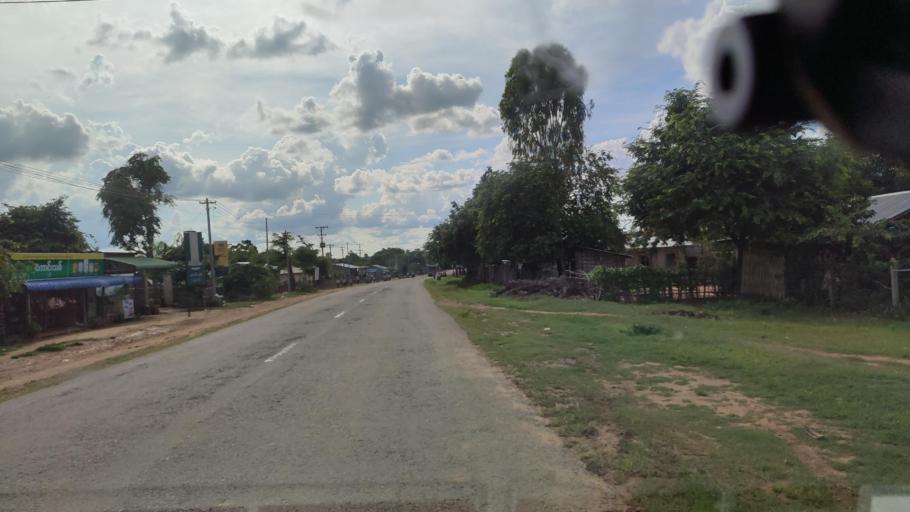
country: MM
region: Mandalay
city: Meiktila
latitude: 20.7897
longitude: 95.5193
